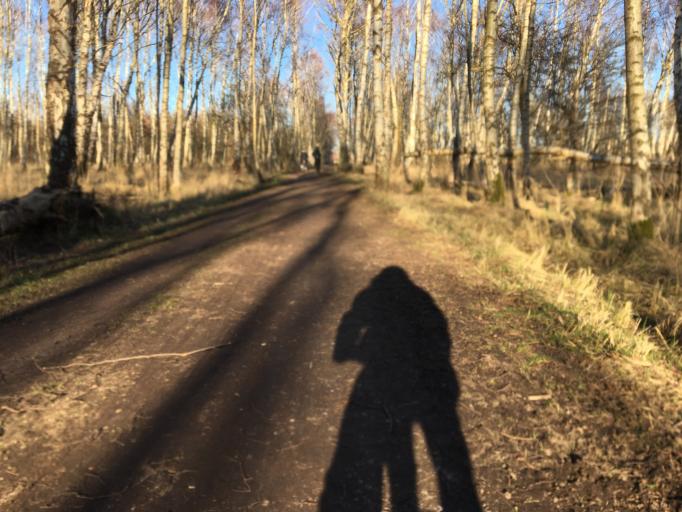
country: DK
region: Capital Region
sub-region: Tarnby Kommune
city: Tarnby
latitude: 55.5894
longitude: 12.5642
